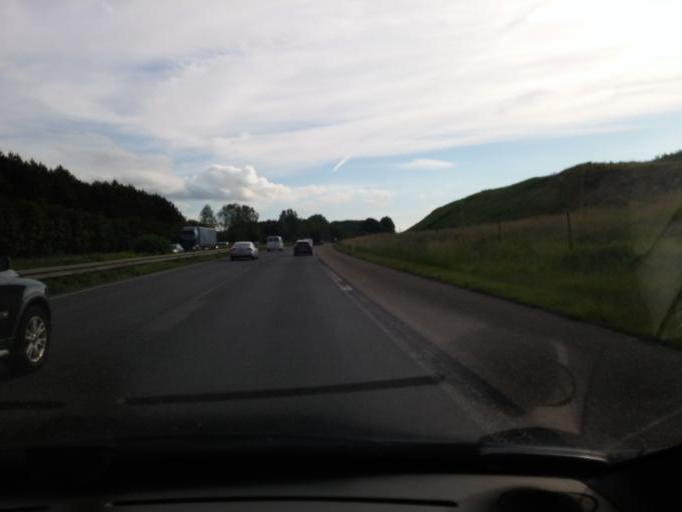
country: DK
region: Zealand
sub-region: Slagelse Kommune
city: Slagelse
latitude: 55.4057
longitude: 11.4027
